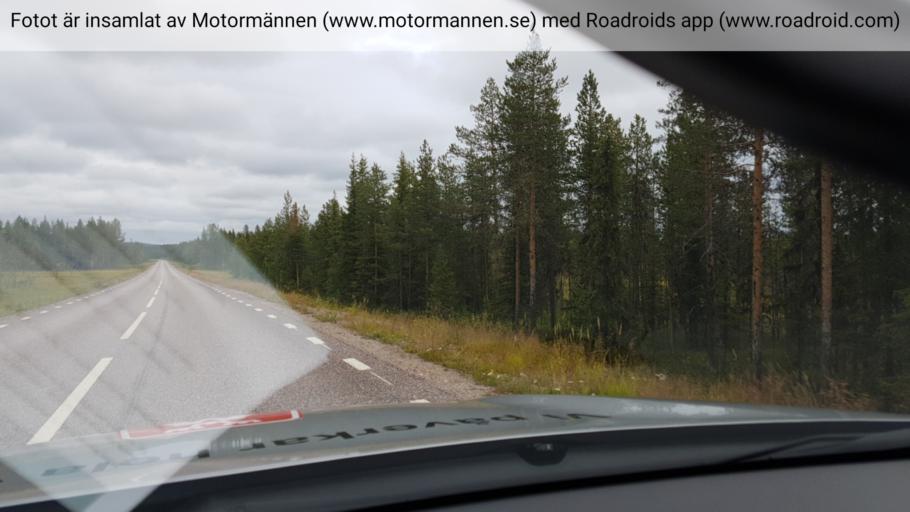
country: SE
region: Norrbotten
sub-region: Gallivare Kommun
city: Gaellivare
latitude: 67.0558
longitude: 21.2446
